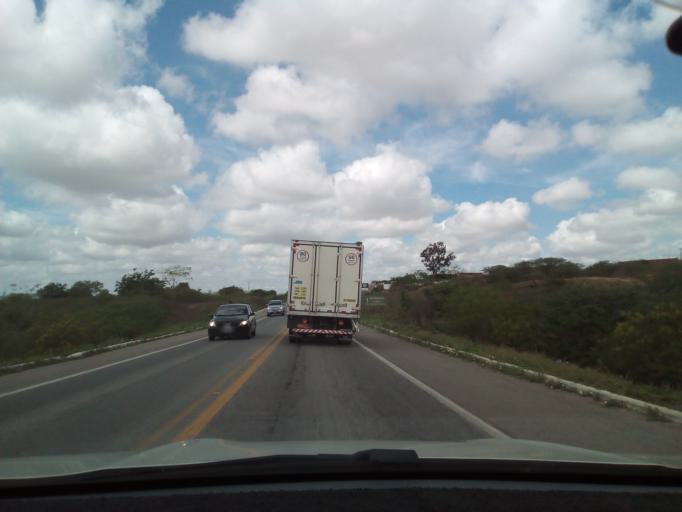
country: BR
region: Paraiba
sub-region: Campina Grande
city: Campina Grande
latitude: -7.2687
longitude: -35.8836
